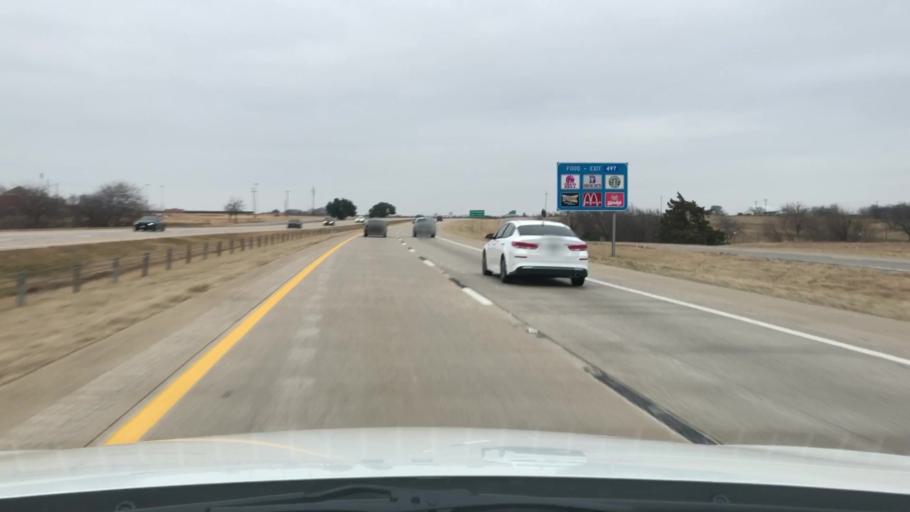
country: US
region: Texas
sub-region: Cooke County
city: Gainesville
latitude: 33.6006
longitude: -97.1606
